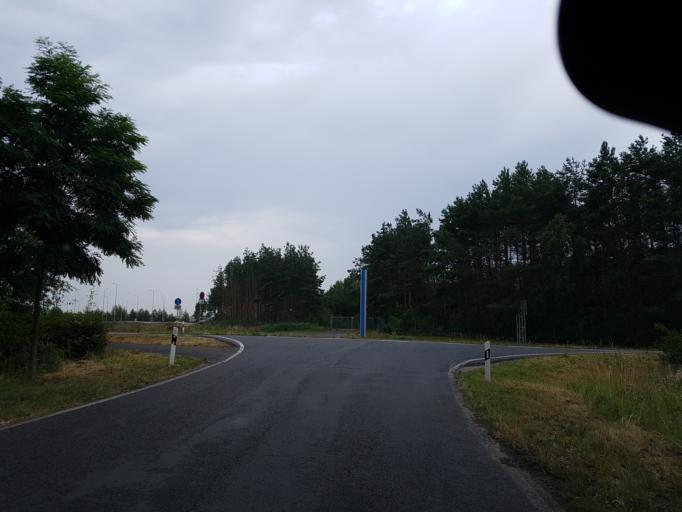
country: DE
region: Brandenburg
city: Schipkau
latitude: 51.5453
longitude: 13.9252
